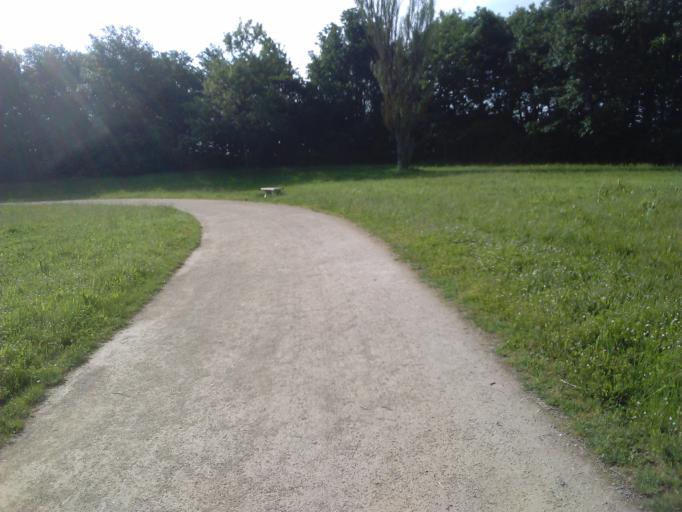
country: FR
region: Centre
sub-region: Departement du Loir-et-Cher
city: Villiers-sur-Loir
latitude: 47.7971
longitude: 0.9887
